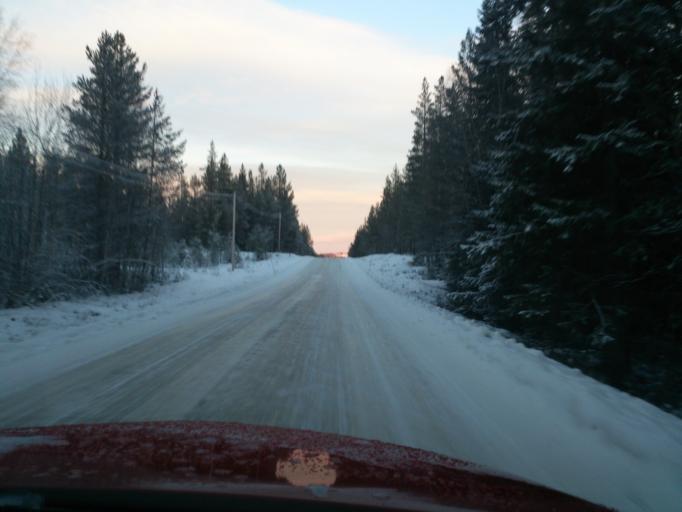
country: SE
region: Jaemtland
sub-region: Harjedalens Kommun
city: Sveg
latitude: 62.3865
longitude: 13.4958
